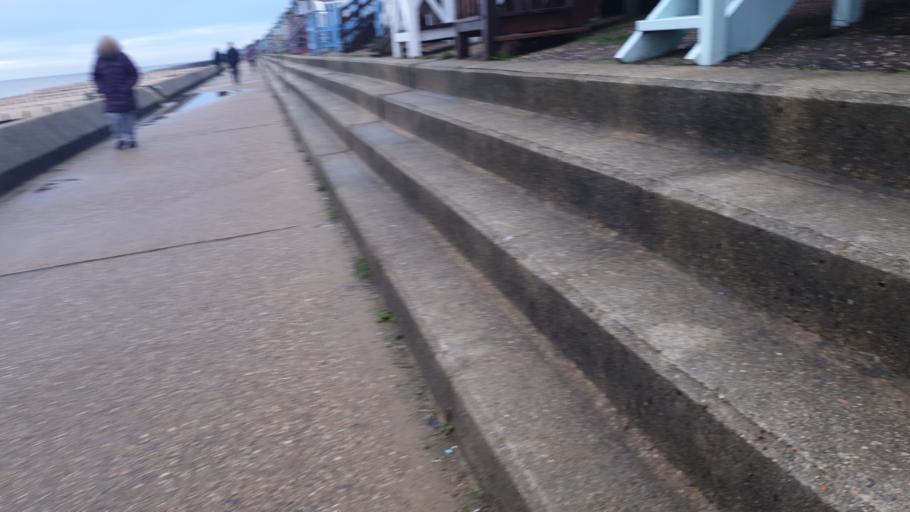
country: GB
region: England
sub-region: Essex
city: Frinton-on-Sea
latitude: 51.8351
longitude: 1.2559
